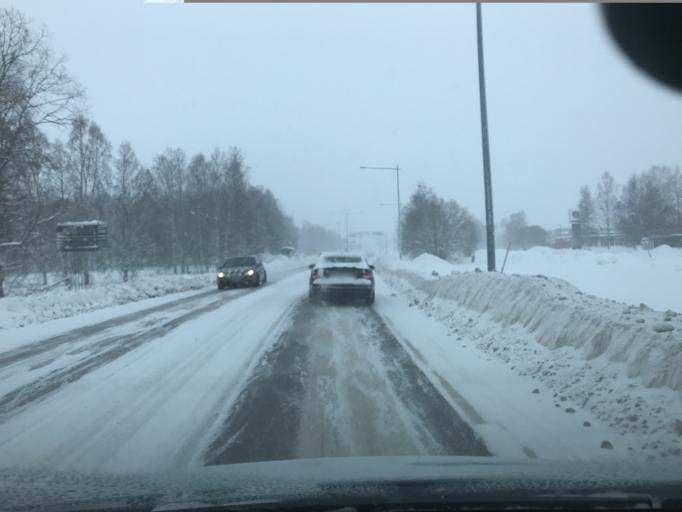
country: SE
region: Norrbotten
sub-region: Lulea Kommun
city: Lulea
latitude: 65.6149
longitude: 22.1326
